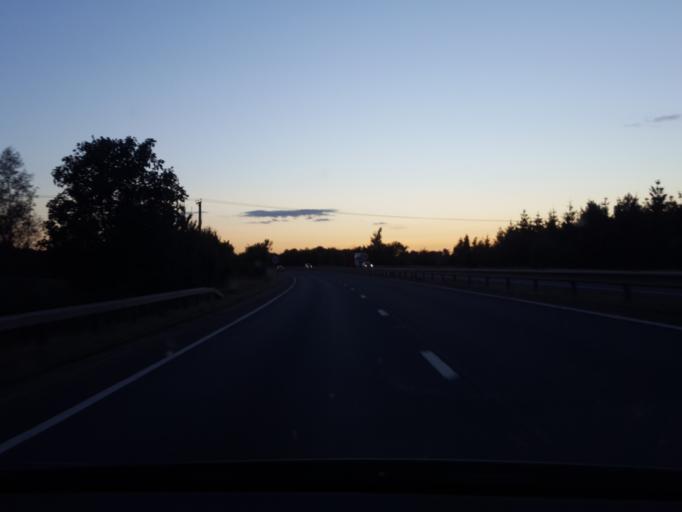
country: GB
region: England
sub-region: Leicestershire
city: Quorndon
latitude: 52.7520
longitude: -1.1738
